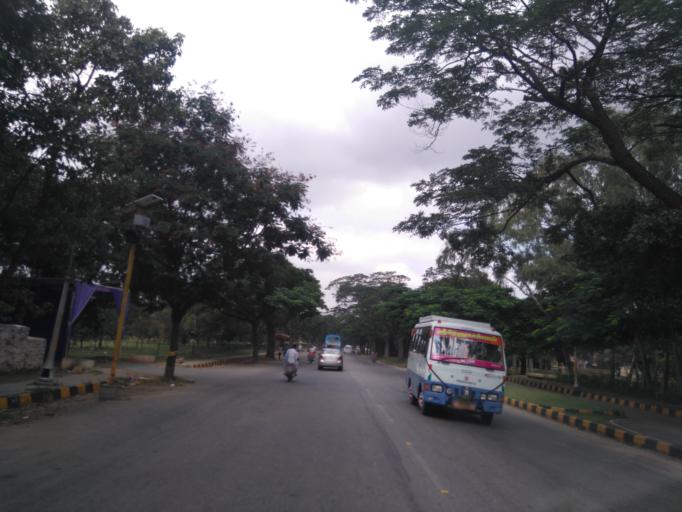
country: IN
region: Karnataka
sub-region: Mysore
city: Mysore
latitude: 12.2985
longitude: 76.6748
